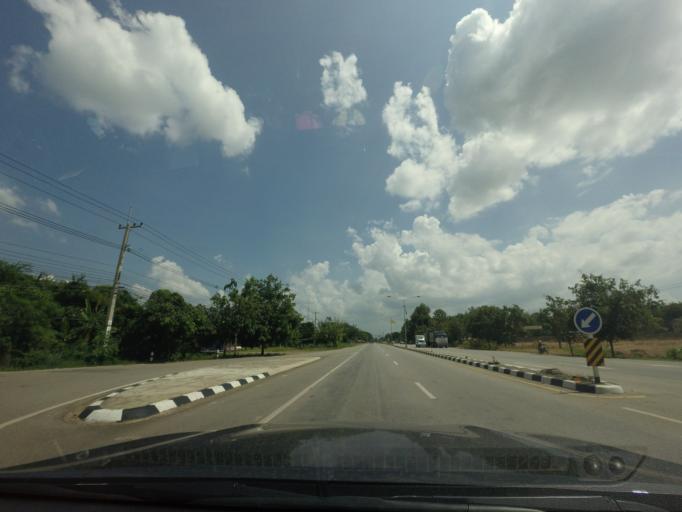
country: TH
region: Phetchabun
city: Phetchabun
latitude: 16.2554
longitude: 101.0609
